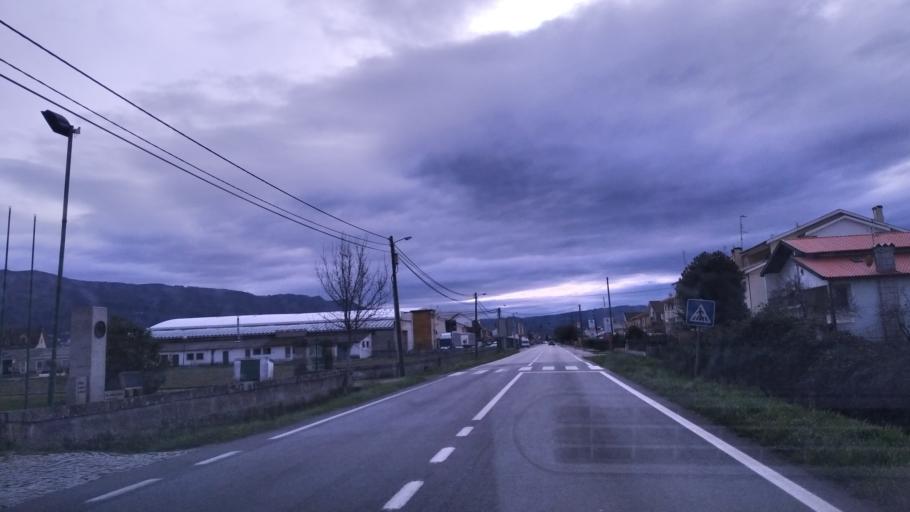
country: PT
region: Vila Real
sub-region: Chaves
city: Chaves
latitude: 41.7406
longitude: -7.4507
